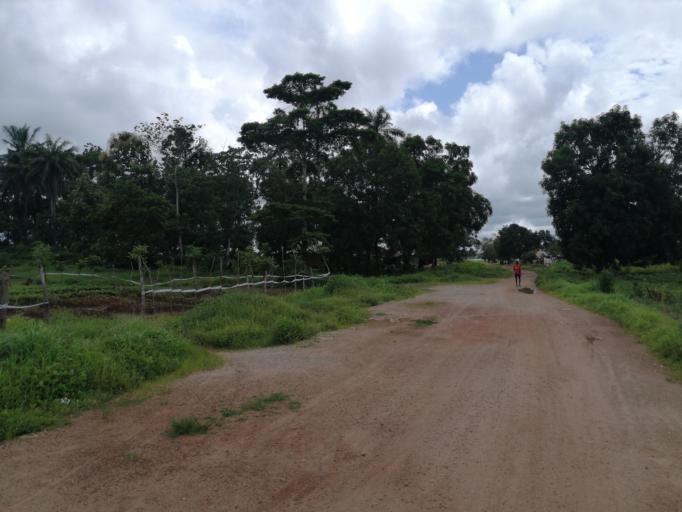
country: SL
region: Northern Province
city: Port Loko
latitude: 8.7839
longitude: -12.7778
